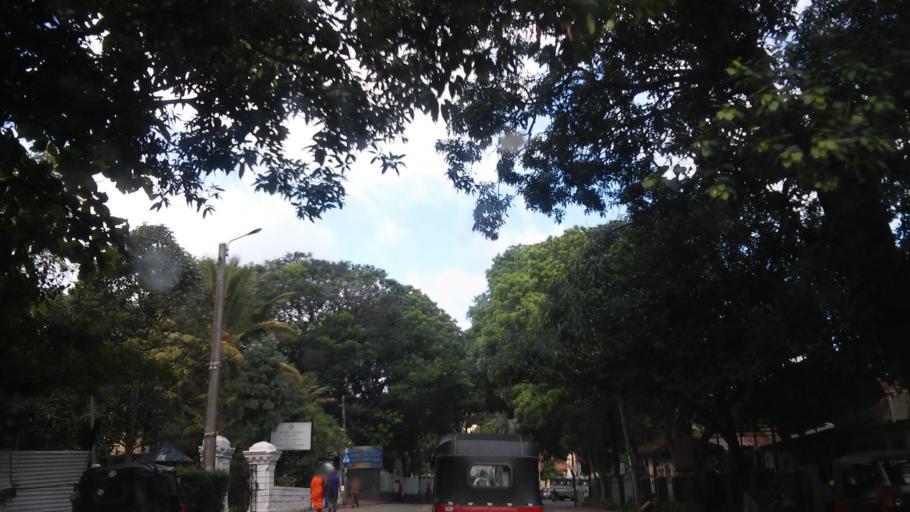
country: LK
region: Central
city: Kandy
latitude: 7.2677
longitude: 80.6021
